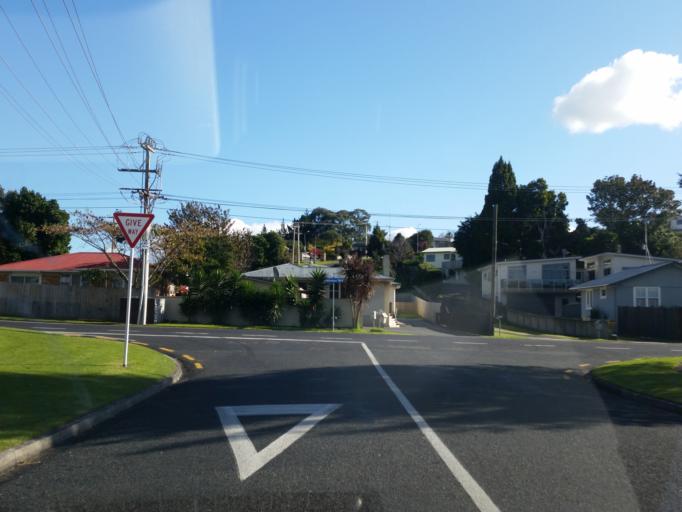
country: NZ
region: Bay of Plenty
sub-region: Tauranga City
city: Tauranga
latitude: -37.6845
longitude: 176.1286
